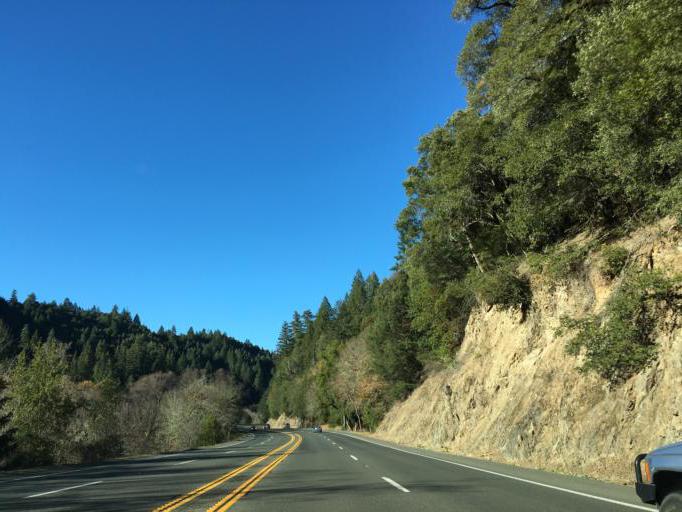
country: US
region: California
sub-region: Mendocino County
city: Brooktrails
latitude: 39.5264
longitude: -123.4006
